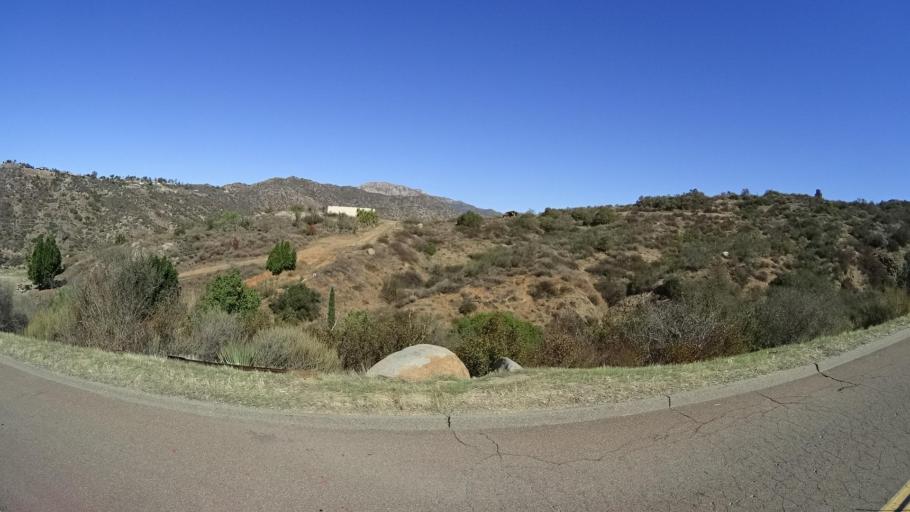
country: US
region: California
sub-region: San Diego County
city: Alpine
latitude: 32.8537
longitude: -116.7983
